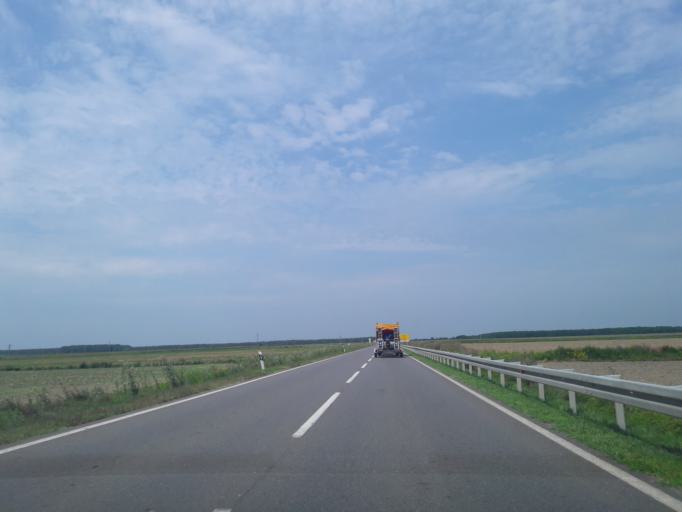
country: HR
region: Osjecko-Baranjska
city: Cepin
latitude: 45.5158
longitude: 18.5278
